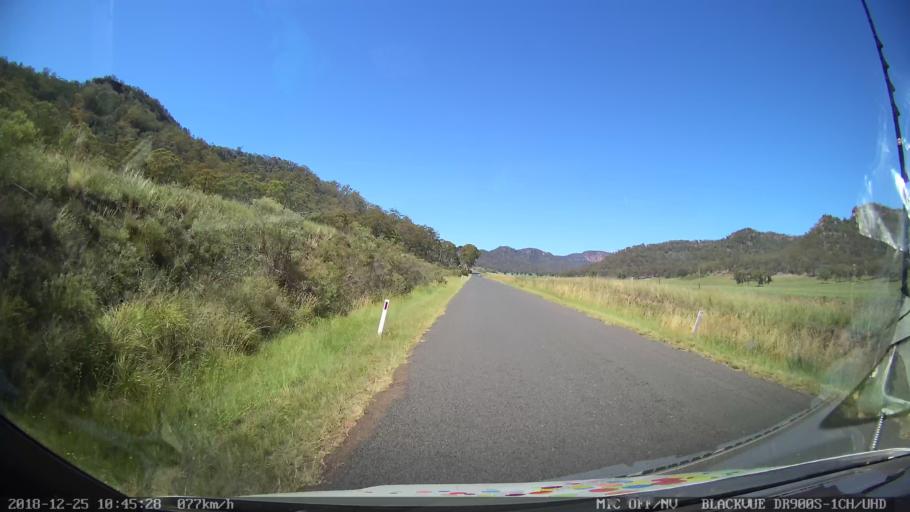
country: AU
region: New South Wales
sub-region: Upper Hunter Shire
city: Merriwa
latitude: -32.4335
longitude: 150.2898
